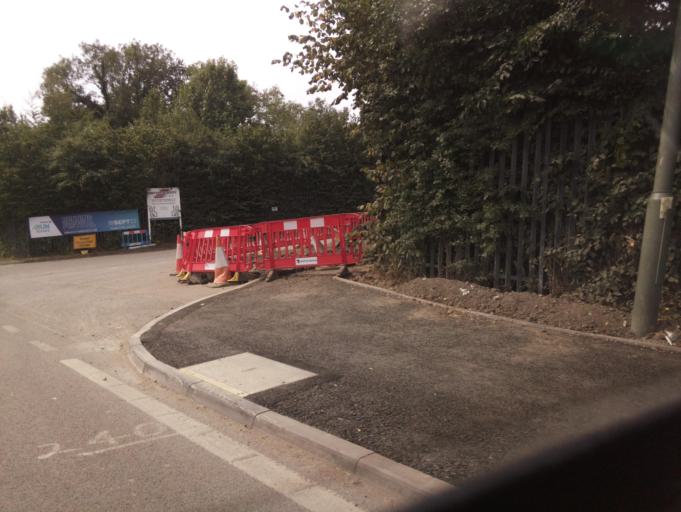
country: GB
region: England
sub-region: Surrey
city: Salfords
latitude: 51.1863
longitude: -0.1959
